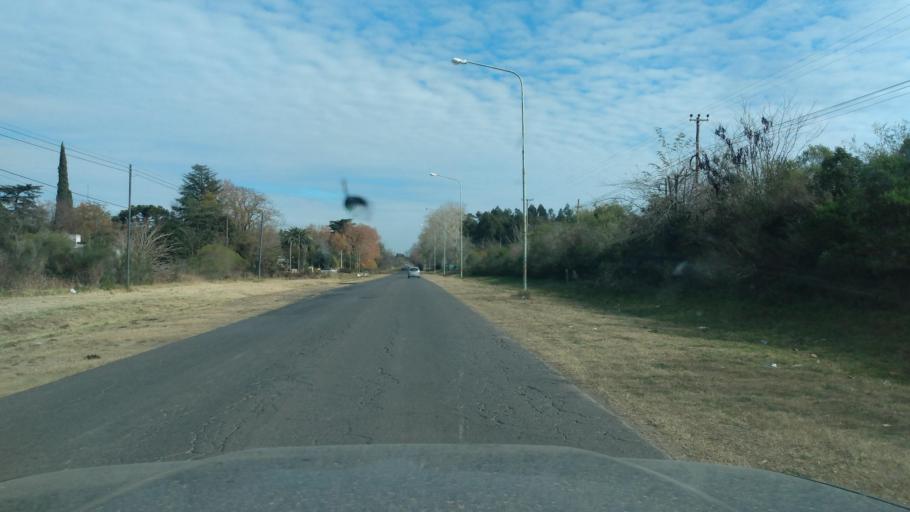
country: AR
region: Buenos Aires
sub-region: Partido de Lujan
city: Lujan
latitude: -34.5714
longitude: -59.1552
